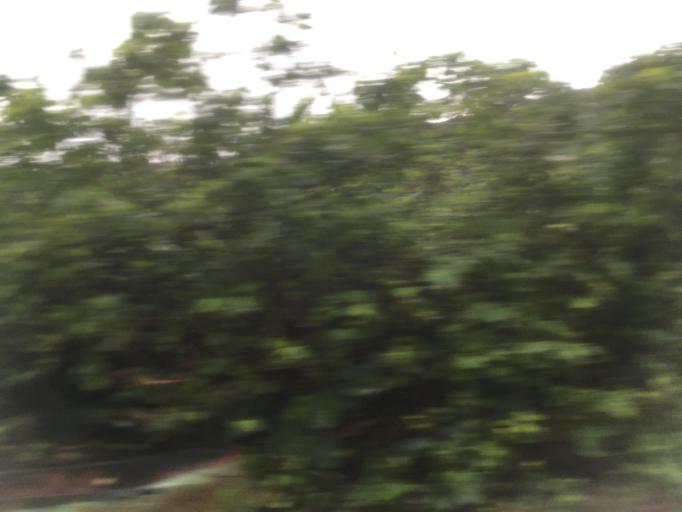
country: TW
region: Taiwan
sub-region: Keelung
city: Keelung
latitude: 25.1119
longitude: 121.9148
